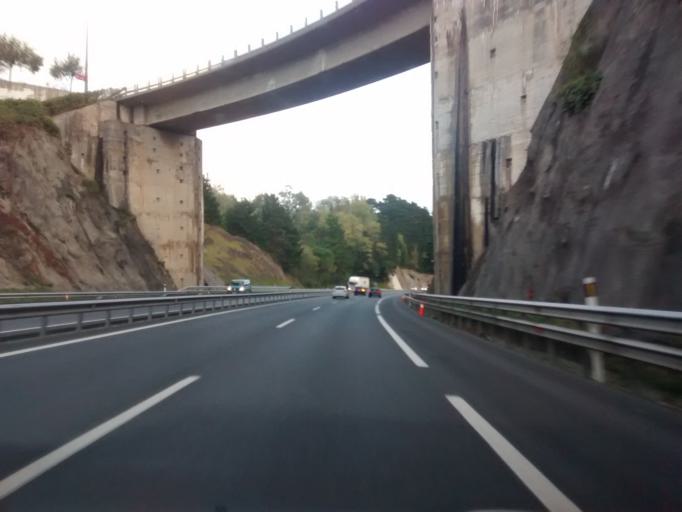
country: ES
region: Basque Country
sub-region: Provincia de Guipuzcoa
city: Deba
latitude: 43.2794
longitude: -2.3128
